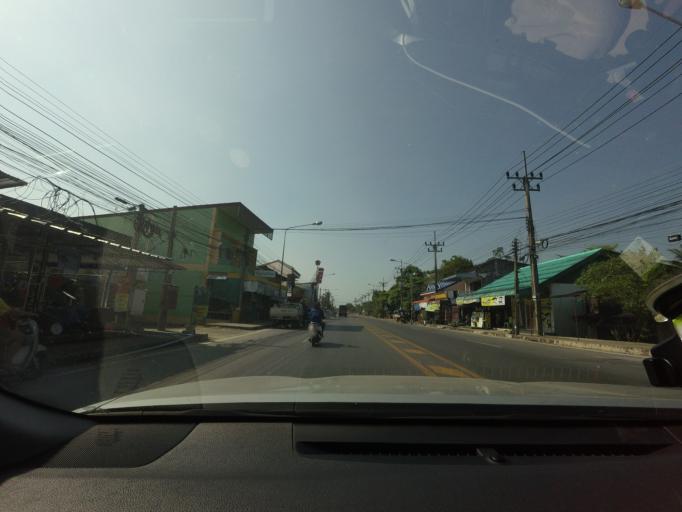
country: TH
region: Nakhon Si Thammarat
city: Chaloem Phra Kiat
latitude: 8.2494
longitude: 100.0133
